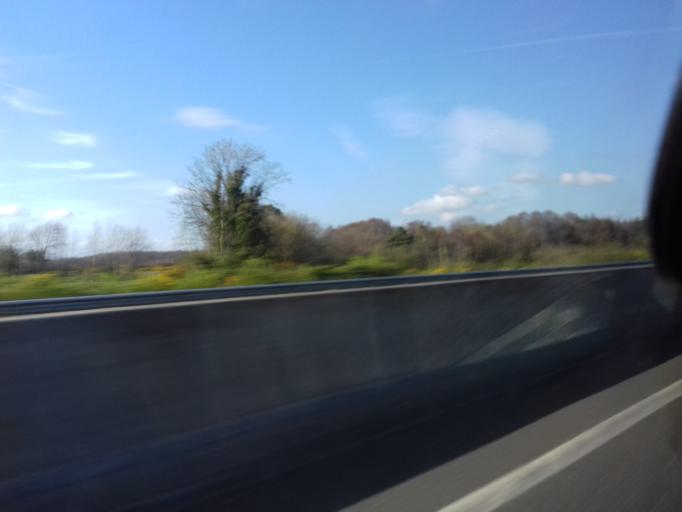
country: IE
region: Leinster
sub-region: Laois
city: Portlaoise
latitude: 53.0084
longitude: -7.3794
